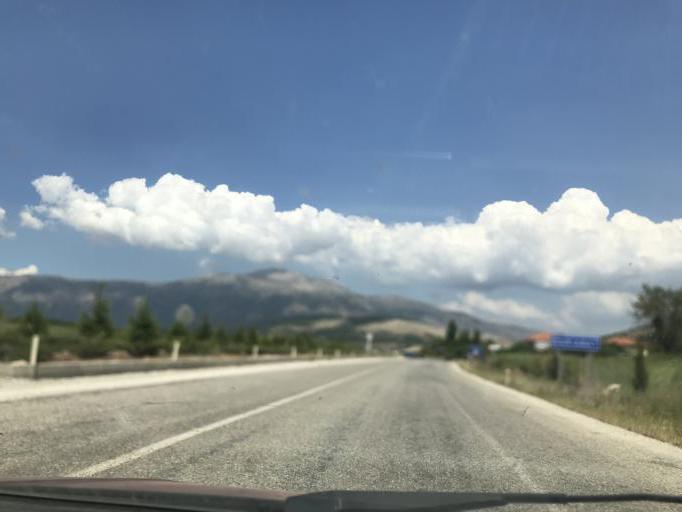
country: TR
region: Denizli
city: Serinhisar
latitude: 37.6195
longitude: 29.1906
